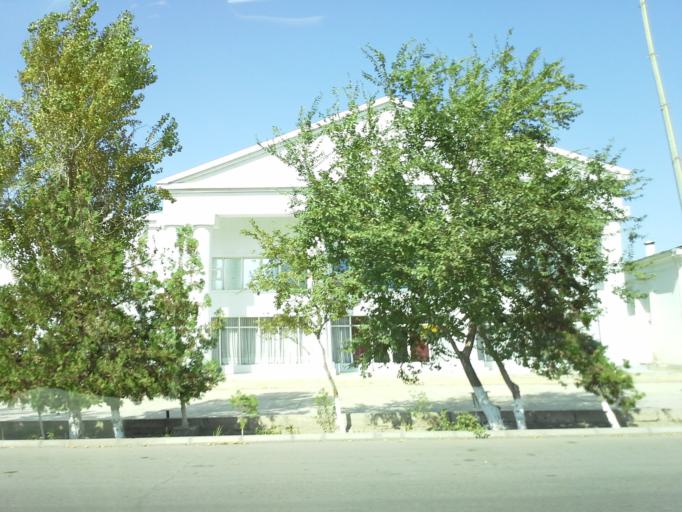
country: TM
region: Dasoguz
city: Dasoguz
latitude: 41.8350
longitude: 59.9639
